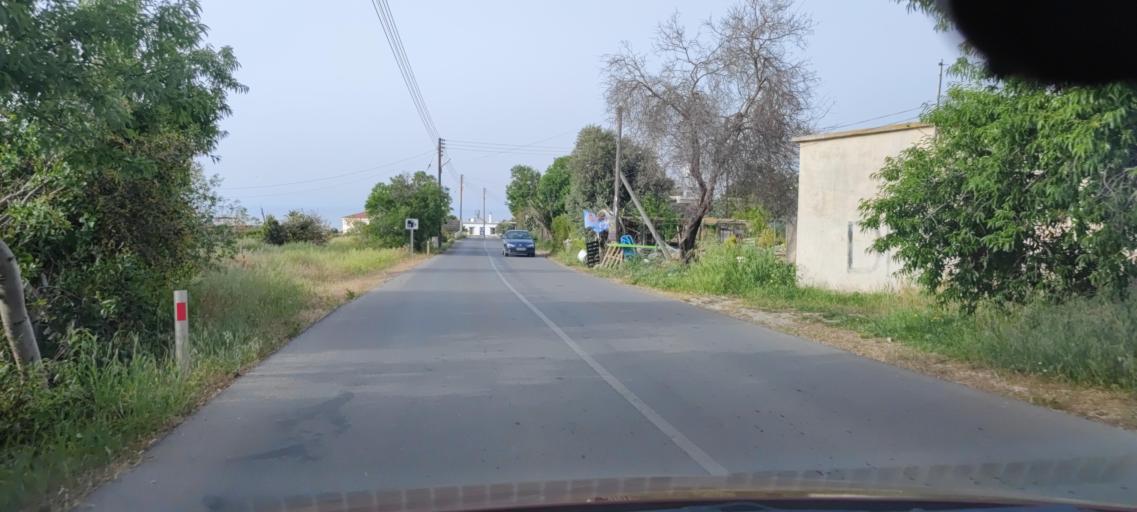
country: CY
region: Ammochostos
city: Leonarisso
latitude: 35.5387
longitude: 34.1934
